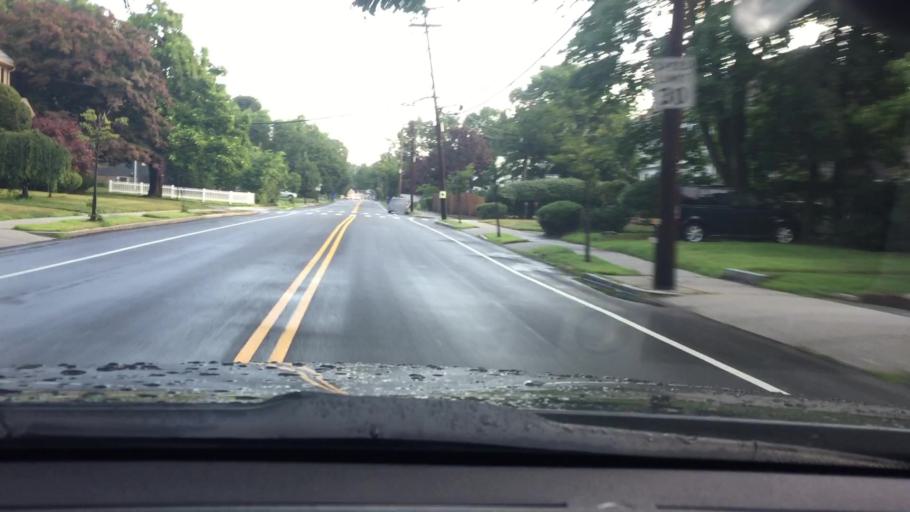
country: US
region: Massachusetts
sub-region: Middlesex County
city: Newton
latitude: 42.3130
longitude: -71.2092
